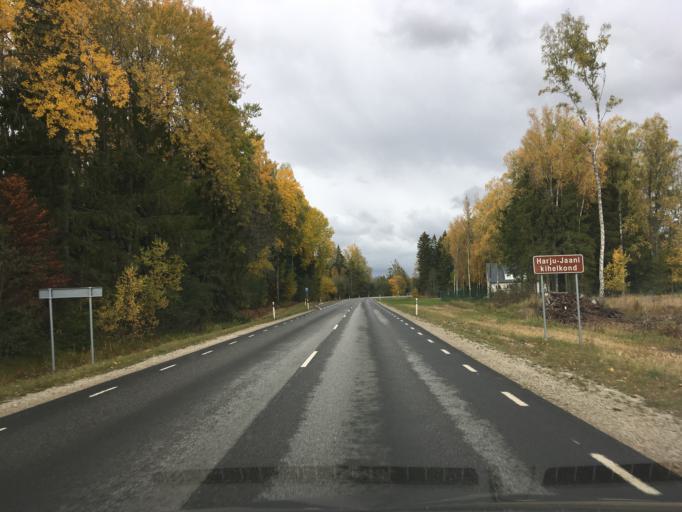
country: EE
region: Harju
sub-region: Anija vald
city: Kehra
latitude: 59.2979
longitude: 25.3657
